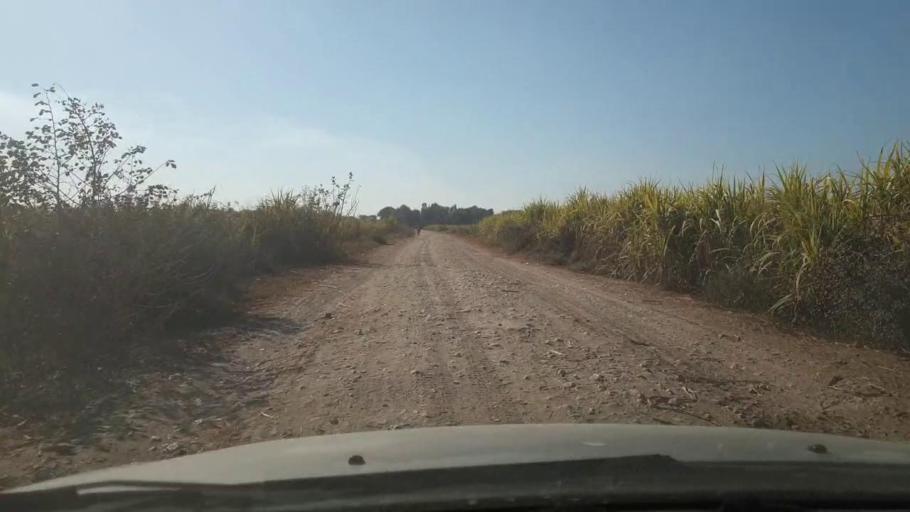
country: PK
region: Sindh
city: Ghotki
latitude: 27.9769
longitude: 69.1909
